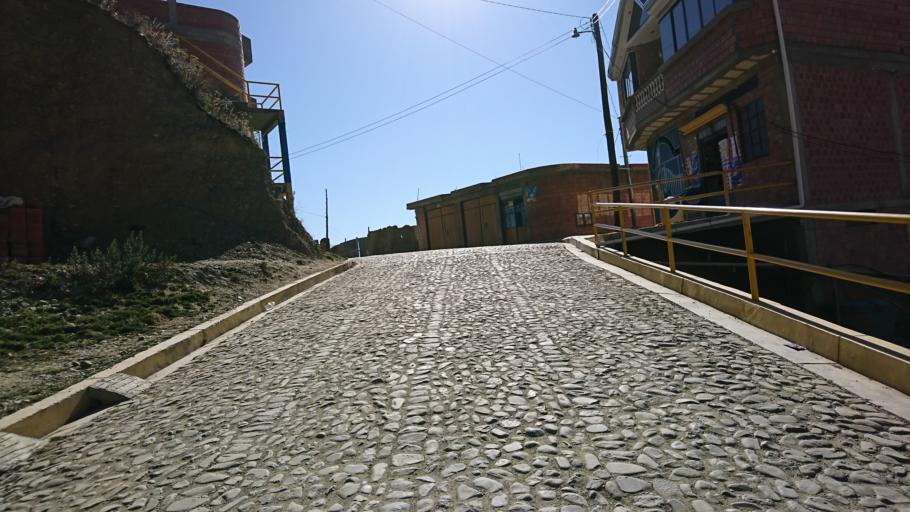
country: BO
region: La Paz
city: La Paz
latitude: -16.4711
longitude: -68.1256
